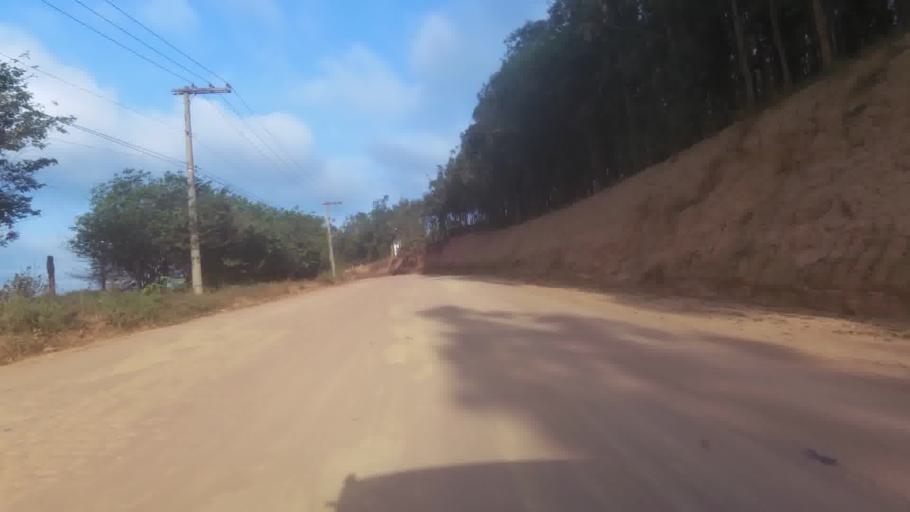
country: BR
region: Espirito Santo
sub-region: Itapemirim
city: Itapemirim
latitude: -21.0205
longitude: -40.8259
